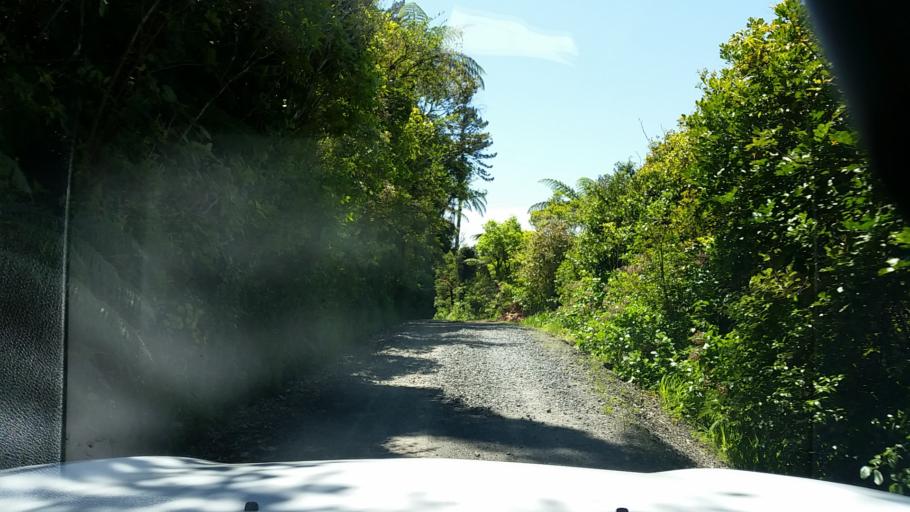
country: NZ
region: Auckland
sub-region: Auckland
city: Titirangi
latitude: -36.9294
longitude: 174.5811
